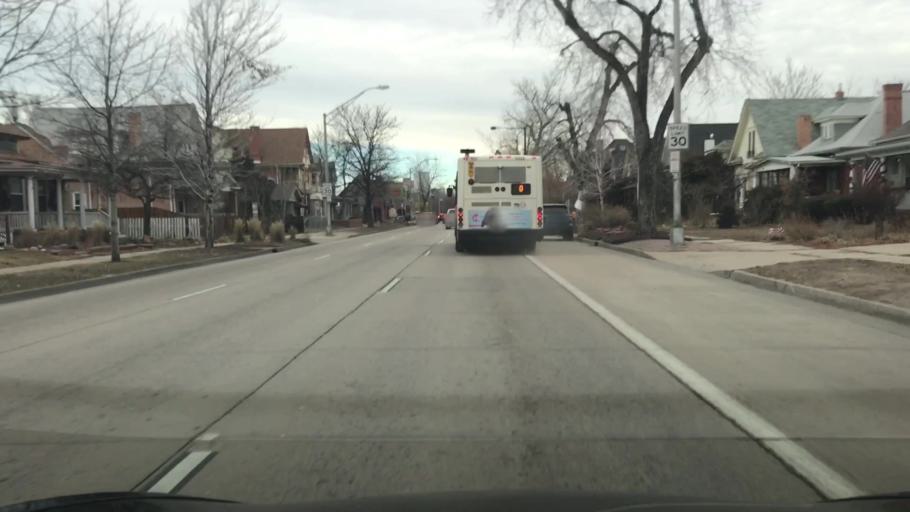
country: US
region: Colorado
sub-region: Denver County
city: Denver
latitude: 39.7081
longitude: -104.9864
